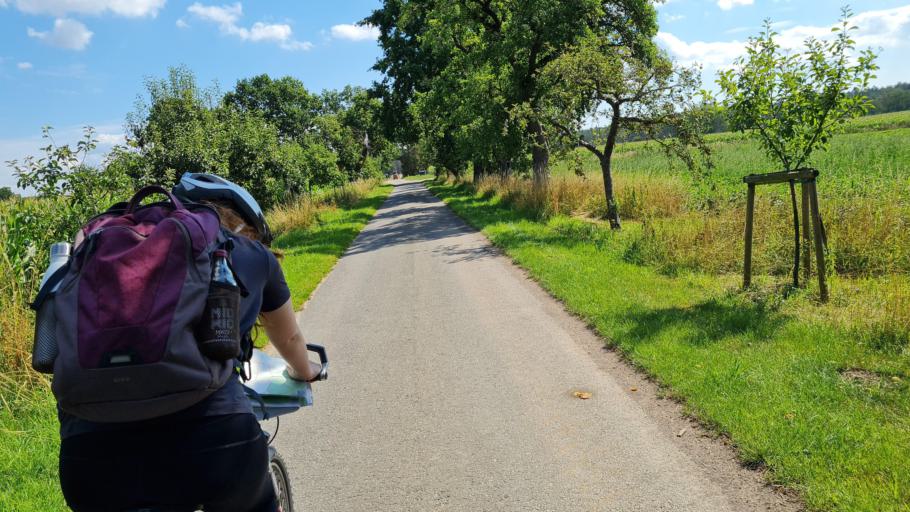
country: DE
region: Lower Saxony
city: Boitze
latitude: 53.1696
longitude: 10.7605
